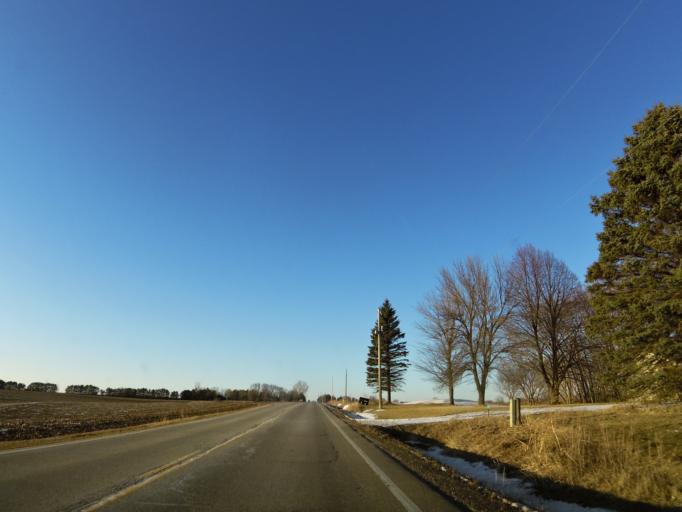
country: US
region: Minnesota
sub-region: Dakota County
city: Hastings
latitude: 44.8003
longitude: -92.8629
